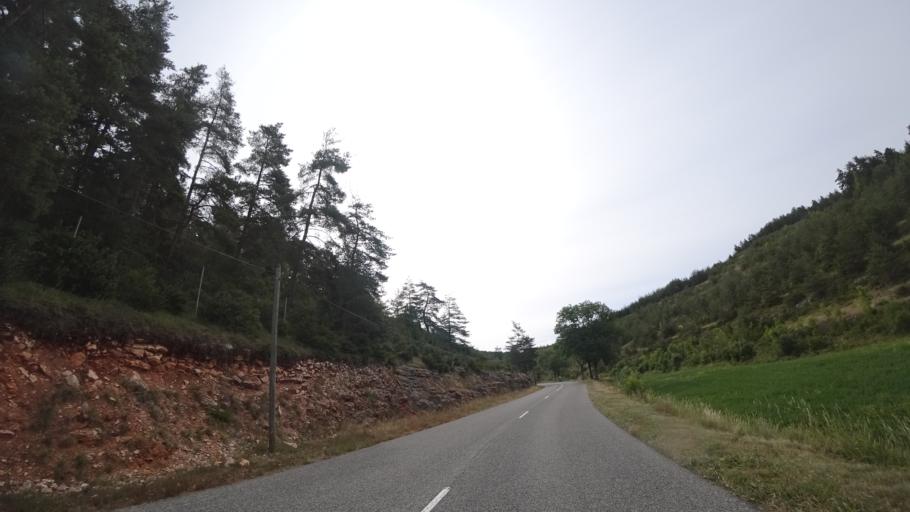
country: FR
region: Languedoc-Roussillon
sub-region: Departement de la Lozere
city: La Canourgue
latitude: 44.4074
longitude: 3.2819
